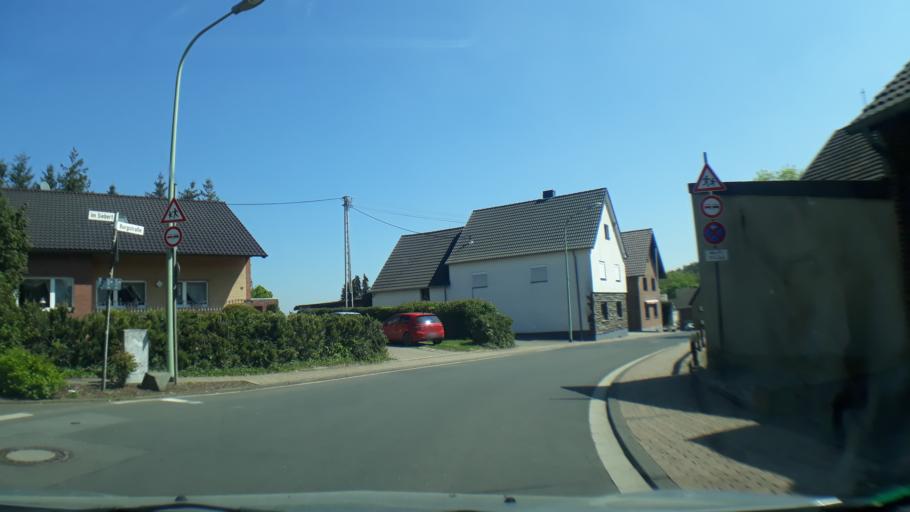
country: DE
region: North Rhine-Westphalia
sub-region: Regierungsbezirk Koln
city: Nideggen
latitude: 50.6961
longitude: 6.4342
